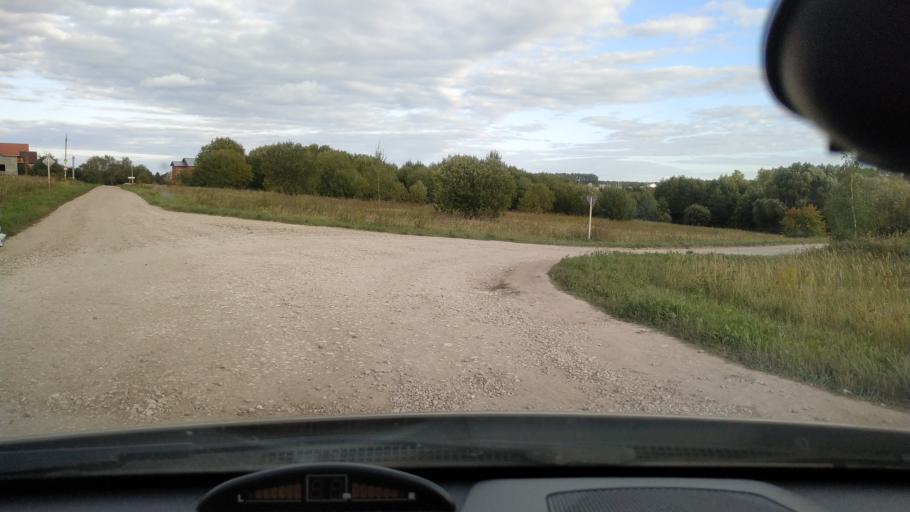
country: RU
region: Rjazan
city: Polyany
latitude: 54.5644
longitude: 39.8741
